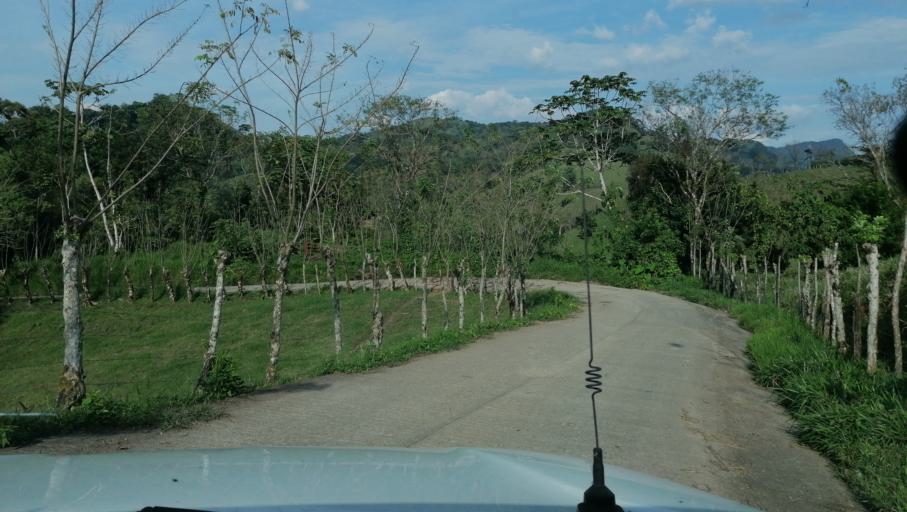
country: MX
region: Chiapas
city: Ostuacan
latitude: 17.4671
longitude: -93.2339
